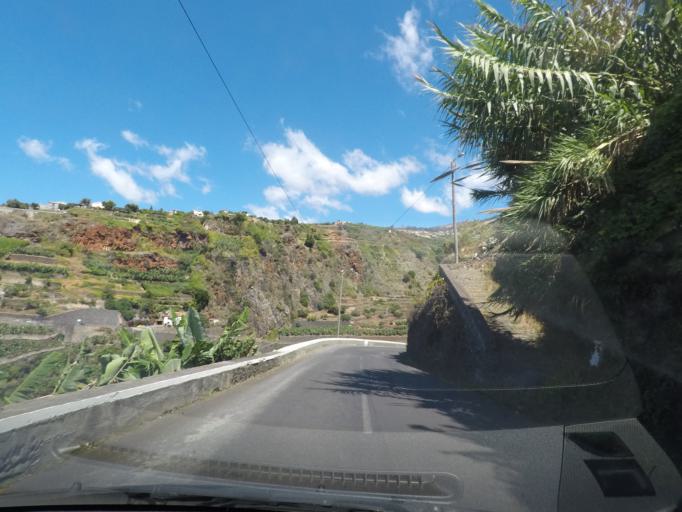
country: PT
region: Madeira
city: Ponta do Sol
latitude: 32.6826
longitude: -17.0996
